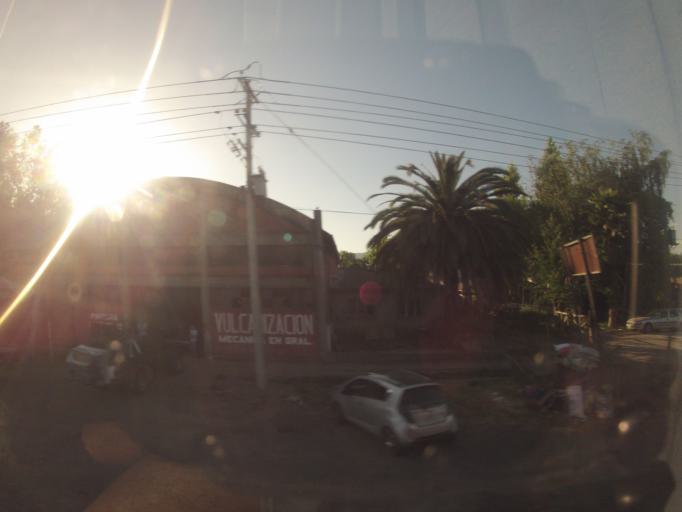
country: CL
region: O'Higgins
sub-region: Provincia de Colchagua
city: Chimbarongo
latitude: -34.7197
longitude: -71.0330
